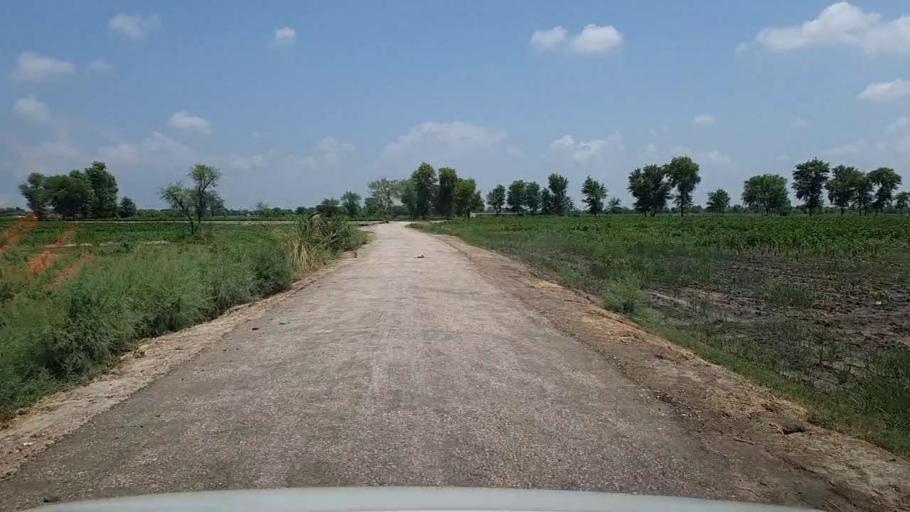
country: PK
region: Sindh
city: Kandiaro
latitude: 26.9862
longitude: 68.2277
